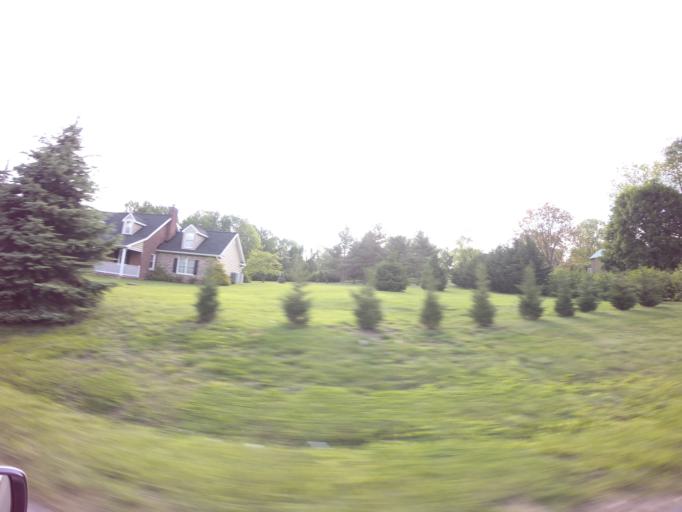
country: US
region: Maryland
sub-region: Baltimore County
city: Cockeysville
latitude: 39.4852
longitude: -76.7079
